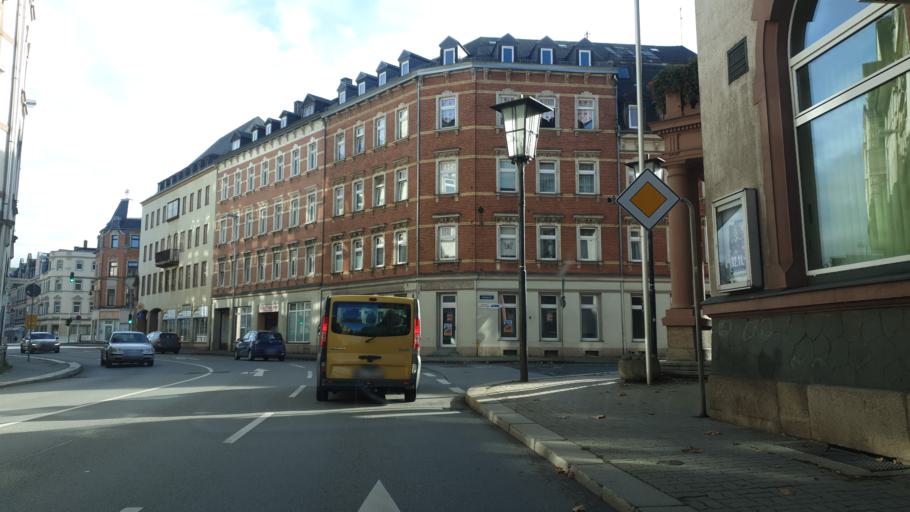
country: DE
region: Saxony
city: Aue
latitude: 50.5873
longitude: 12.6987
